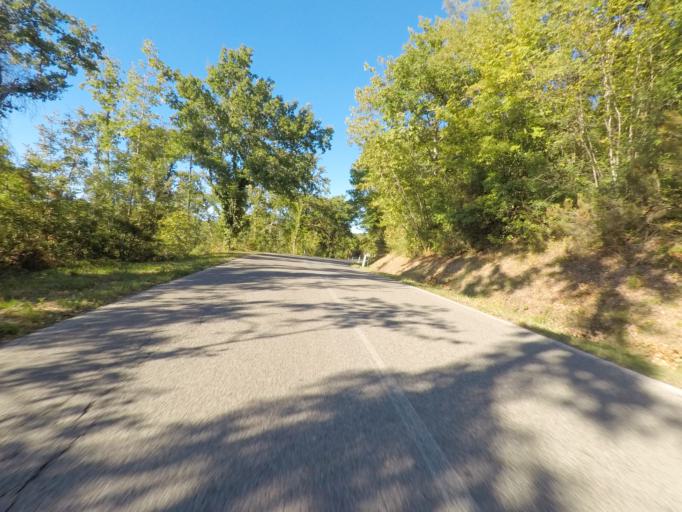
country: IT
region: Tuscany
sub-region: Provincia di Siena
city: Belverde
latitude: 43.3855
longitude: 11.3446
